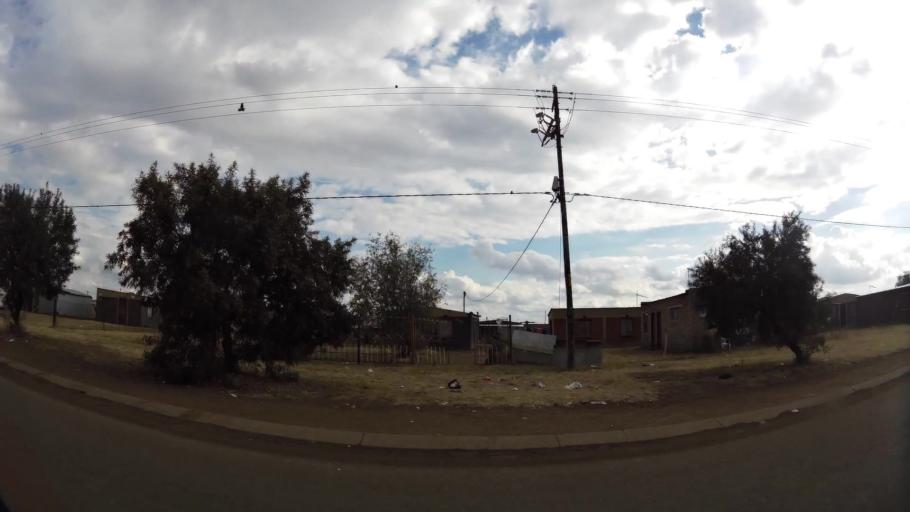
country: ZA
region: Gauteng
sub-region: Sedibeng District Municipality
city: Vanderbijlpark
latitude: -26.6951
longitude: 27.7838
